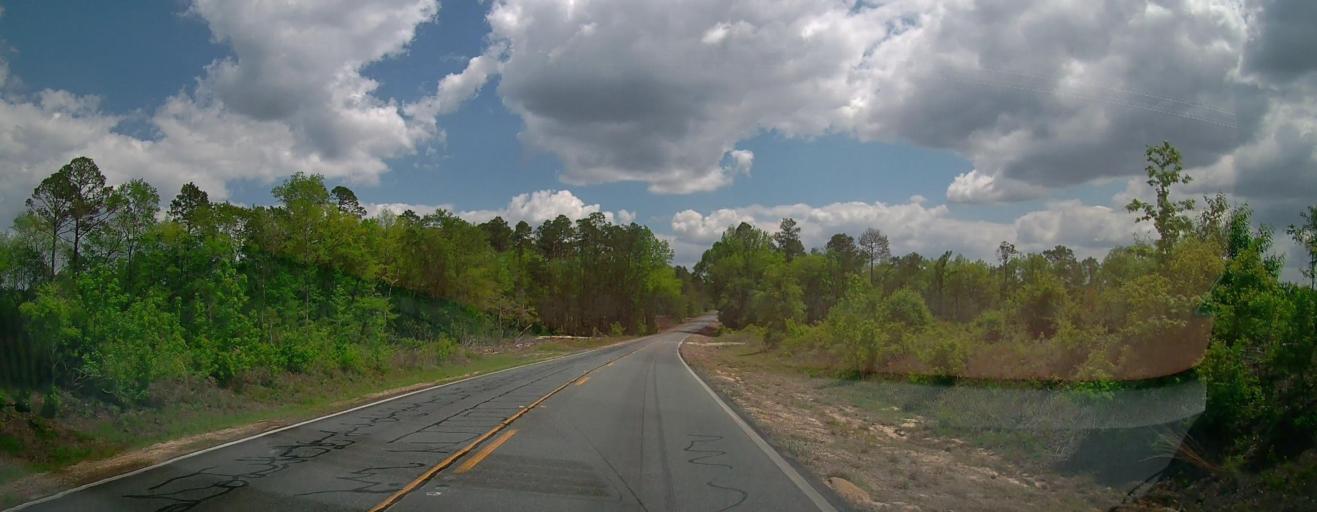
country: US
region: Georgia
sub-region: Treutlen County
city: Soperton
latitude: 32.5005
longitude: -82.6148
